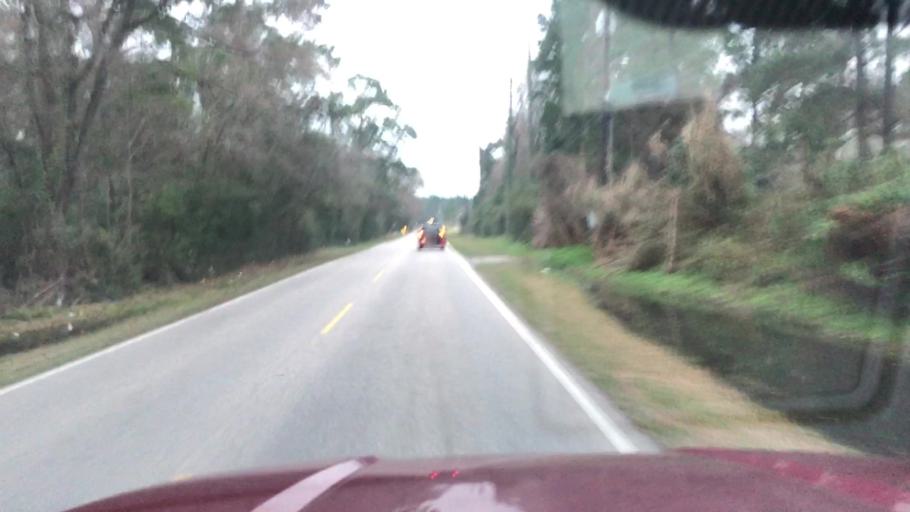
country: US
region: Texas
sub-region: Harris County
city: Tomball
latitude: 30.0840
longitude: -95.5599
